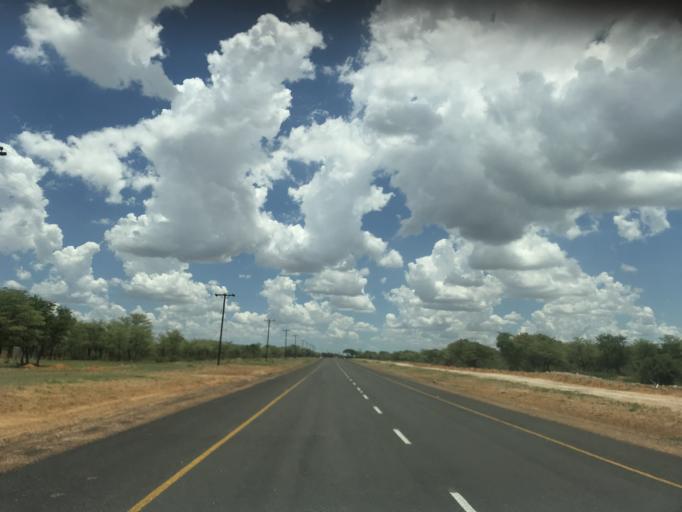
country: BW
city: Mabuli
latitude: -25.8040
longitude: 24.8228
